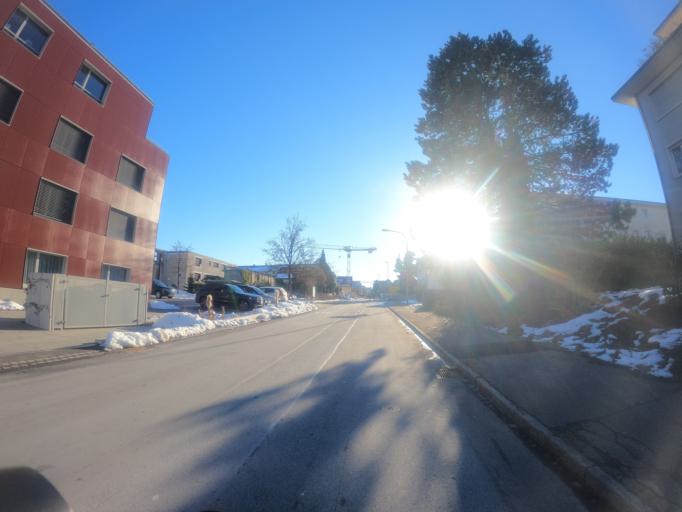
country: CH
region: Zurich
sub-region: Bezirk Affoltern
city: Affoltern / Oberdorf
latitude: 47.2796
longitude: 8.4484
